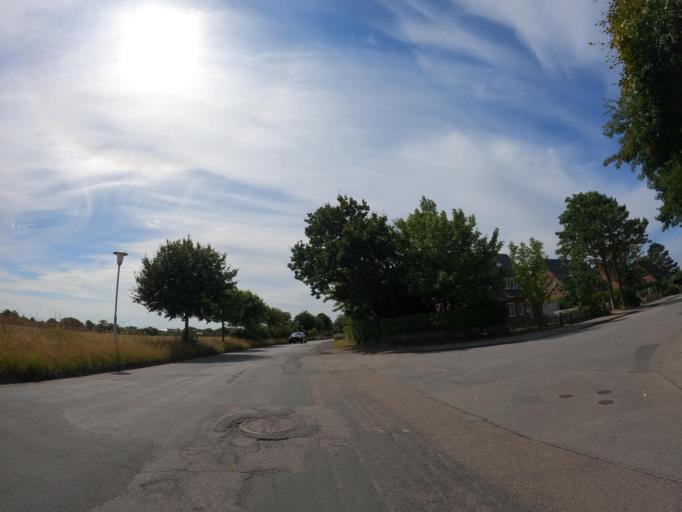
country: DE
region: Schleswig-Holstein
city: Westerland
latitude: 54.9208
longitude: 8.3188
